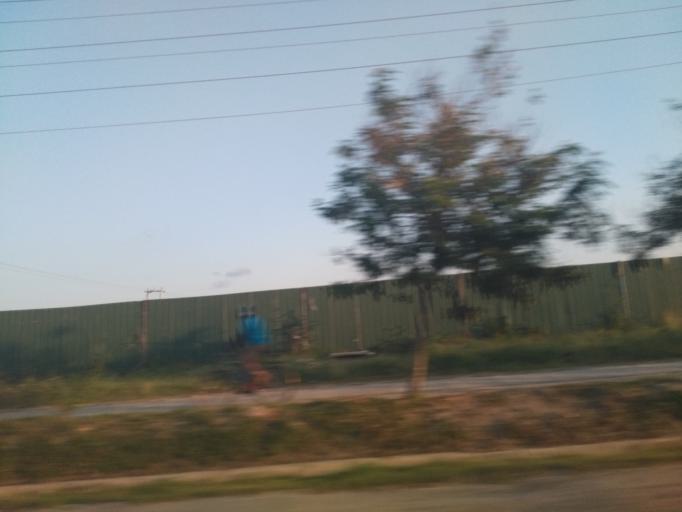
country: TZ
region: Dar es Salaam
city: Dar es Salaam
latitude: -6.8613
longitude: 39.2102
